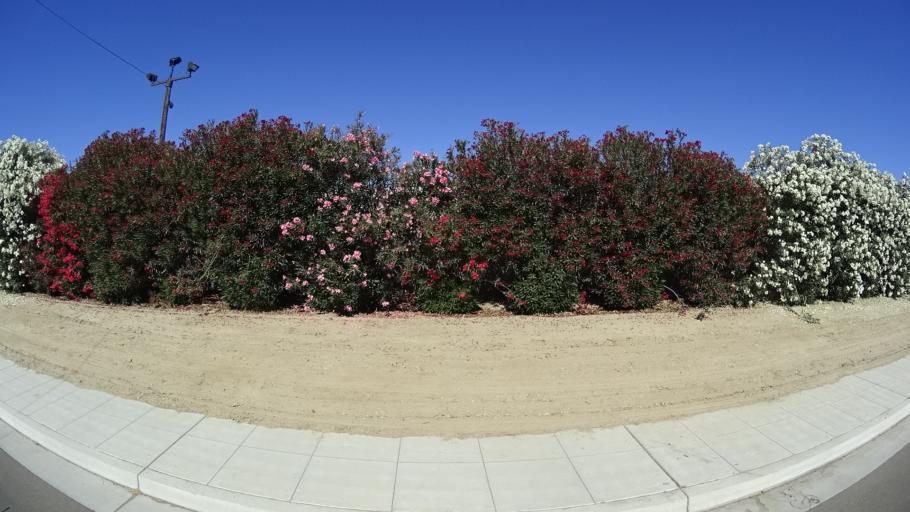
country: US
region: California
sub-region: Fresno County
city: Easton
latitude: 36.6903
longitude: -119.7999
